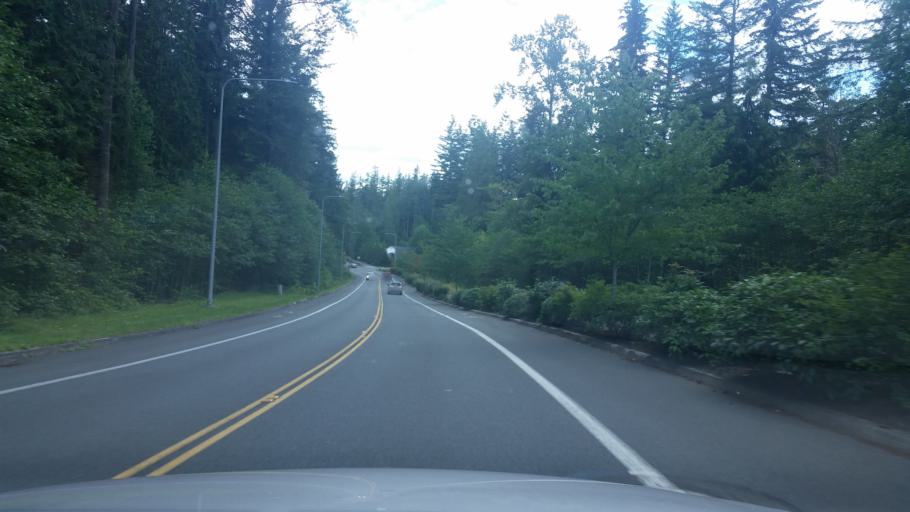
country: US
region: Washington
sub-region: King County
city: Union Hill-Novelty Hill
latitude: 47.7139
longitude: -122.0267
